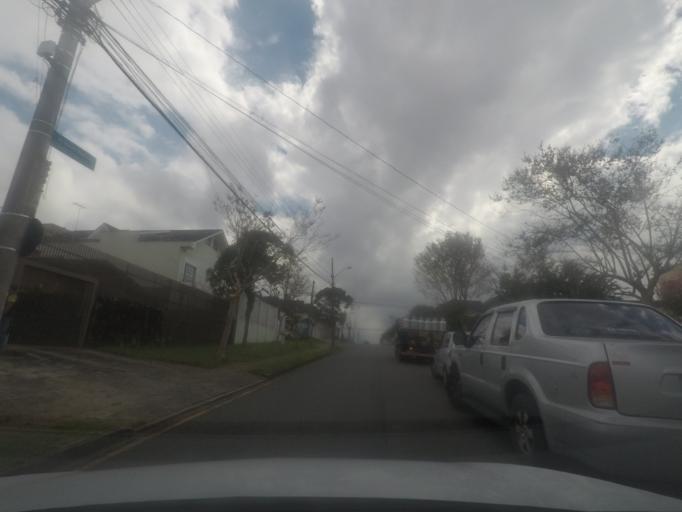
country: BR
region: Parana
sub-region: Curitiba
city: Curitiba
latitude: -25.4571
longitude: -49.2662
